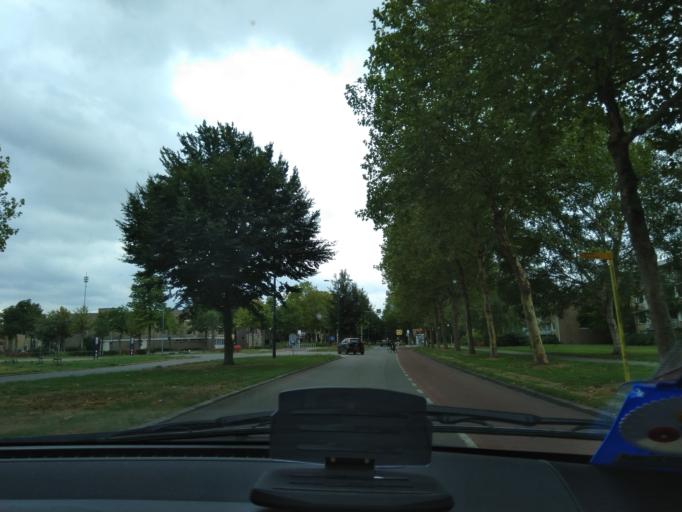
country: NL
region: North Brabant
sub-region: Gemeente Oosterhout
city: Oosterhout
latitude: 51.6249
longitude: 4.8542
